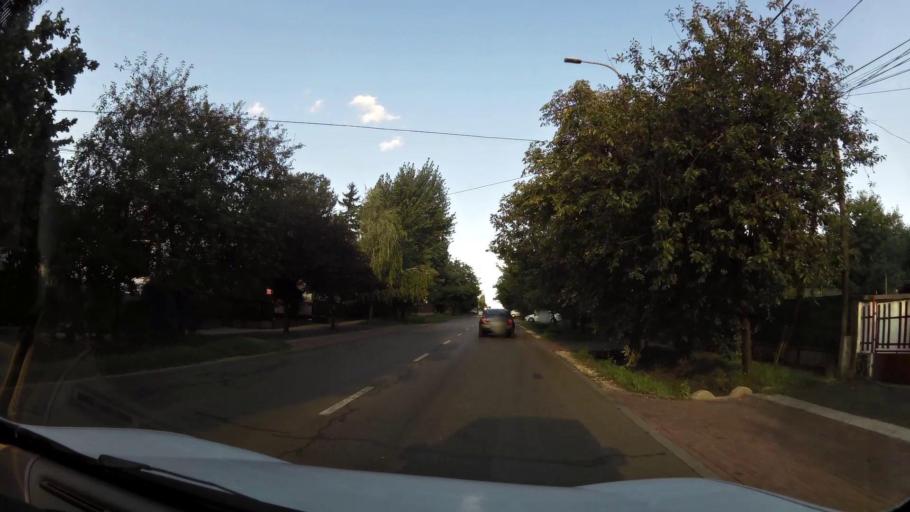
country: HU
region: Budapest
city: Budapest XVI. keruelet
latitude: 47.5039
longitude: 19.1861
